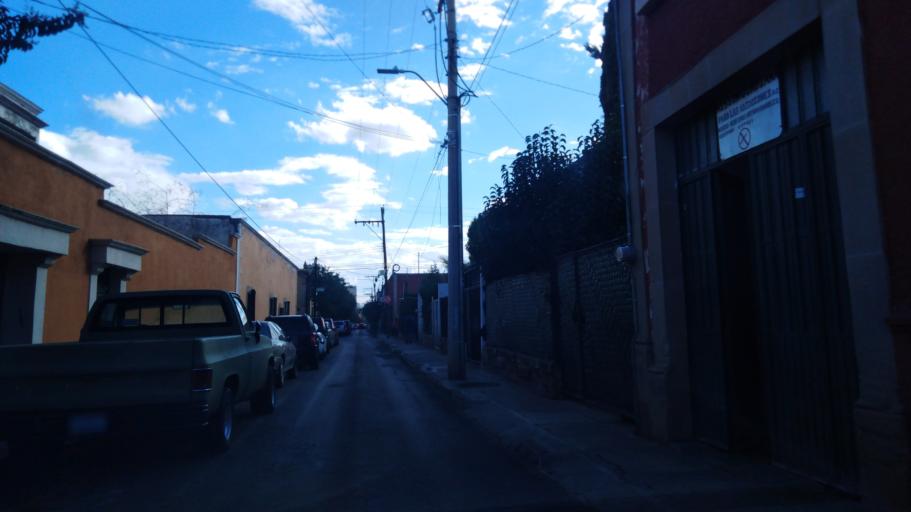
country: MX
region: Durango
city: Victoria de Durango
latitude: 24.0274
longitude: -104.6725
